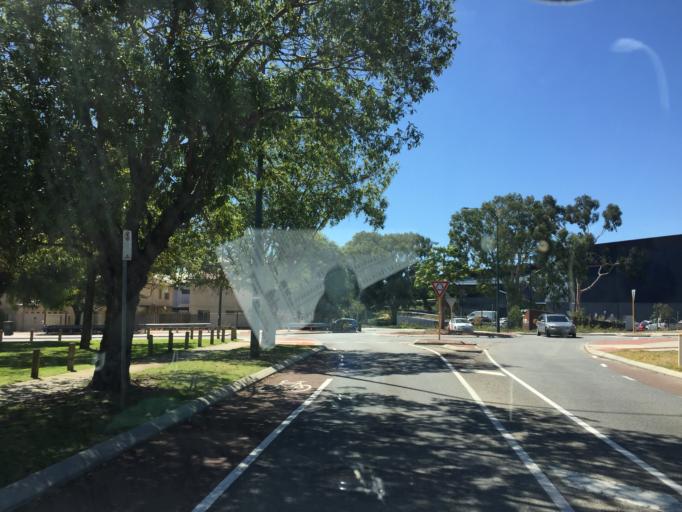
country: AU
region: Western Australia
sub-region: Victoria Park
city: Victoria Park
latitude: -31.9748
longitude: 115.9089
